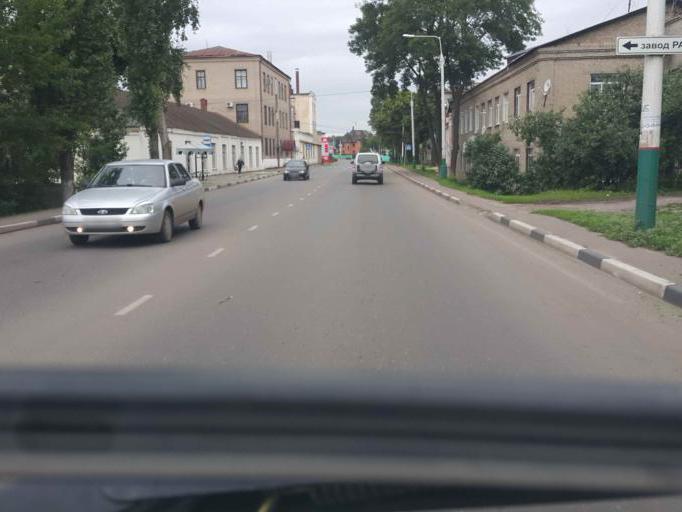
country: RU
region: Tambov
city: Zavoronezhskoye
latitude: 52.8817
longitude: 40.5288
